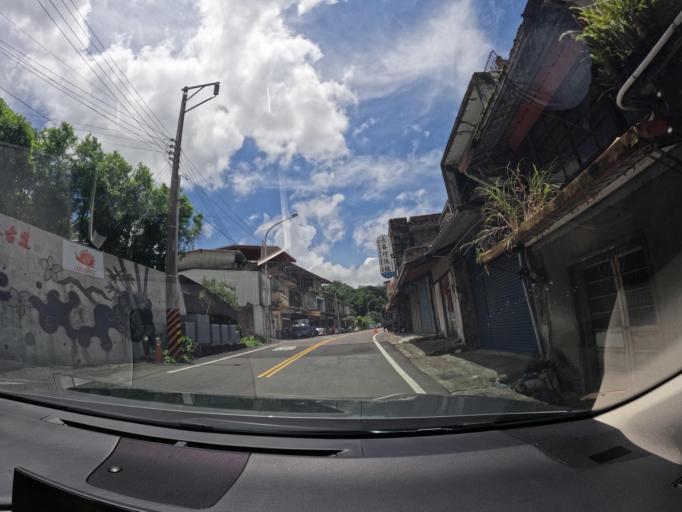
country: TW
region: Taiwan
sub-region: Hsinchu
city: Hsinchu
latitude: 24.6310
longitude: 121.0120
